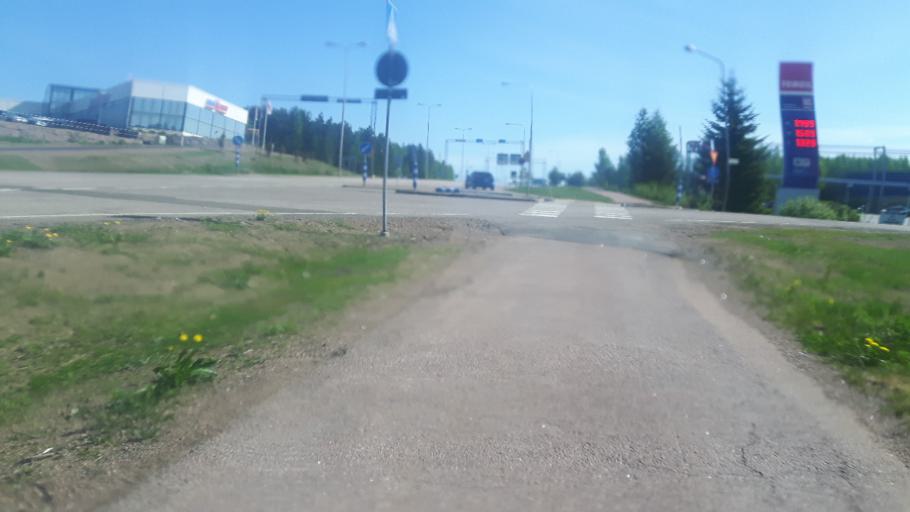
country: FI
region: Kymenlaakso
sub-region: Kotka-Hamina
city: Virojoki
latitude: 60.6017
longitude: 27.8378
